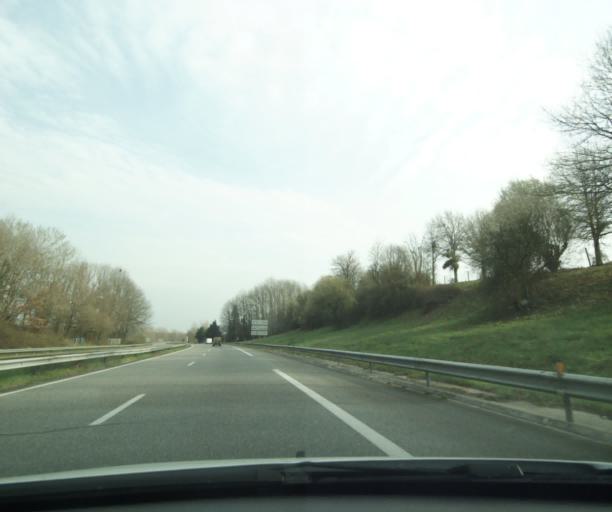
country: FR
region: Aquitaine
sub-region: Departement des Pyrenees-Atlantiques
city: Orthez
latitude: 43.4748
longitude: -0.7635
